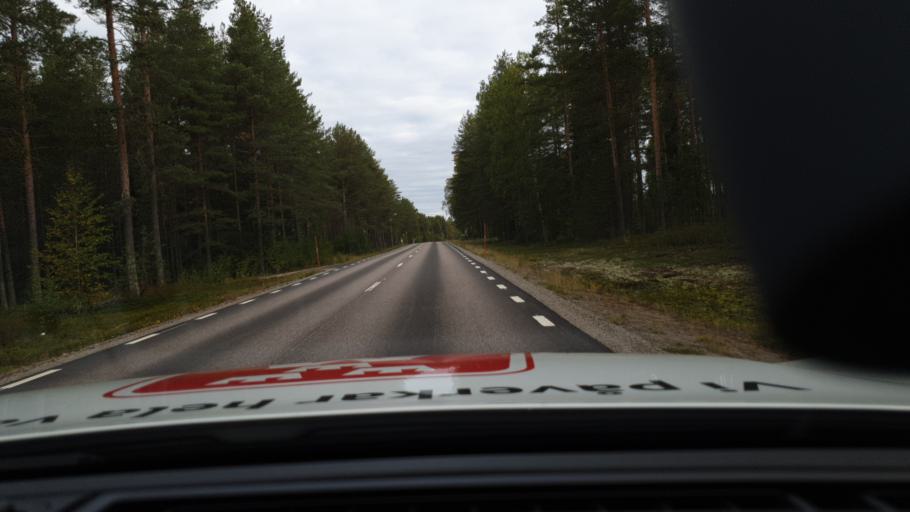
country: SE
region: Norrbotten
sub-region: Overkalix Kommun
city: OEverkalix
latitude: 66.4279
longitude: 22.7956
